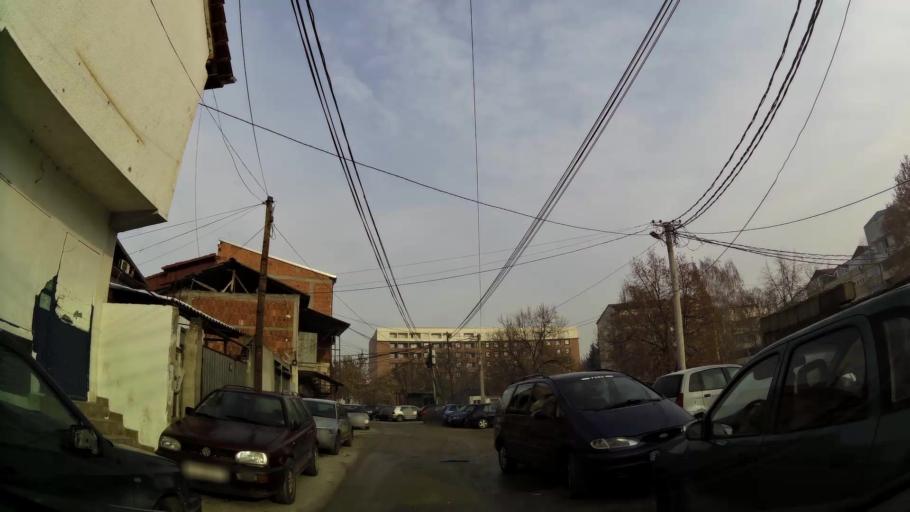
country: MK
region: Cair
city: Cair
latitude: 42.0204
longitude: 21.4387
